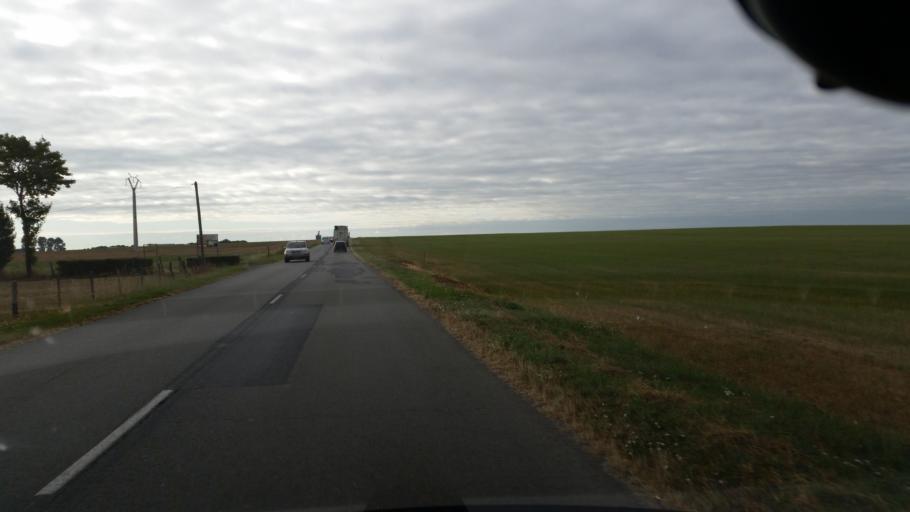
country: FR
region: Poitou-Charentes
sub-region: Departement de la Charente-Maritime
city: Marans
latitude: 46.2974
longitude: -0.9742
